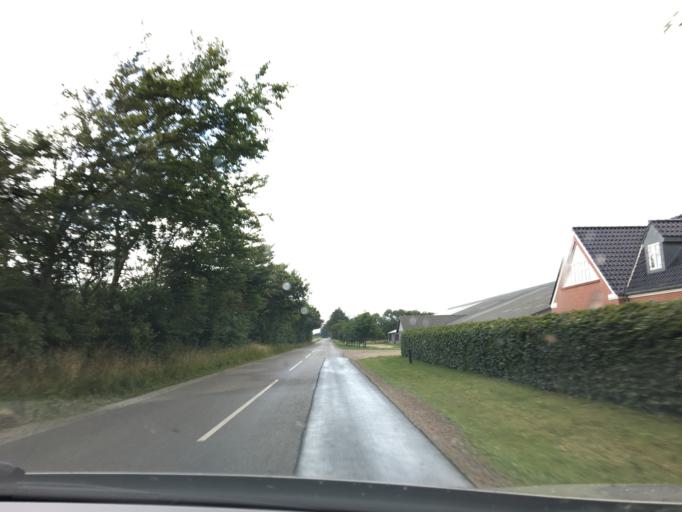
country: DK
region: South Denmark
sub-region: Varde Kommune
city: Oksbol
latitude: 55.6954
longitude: 8.3187
